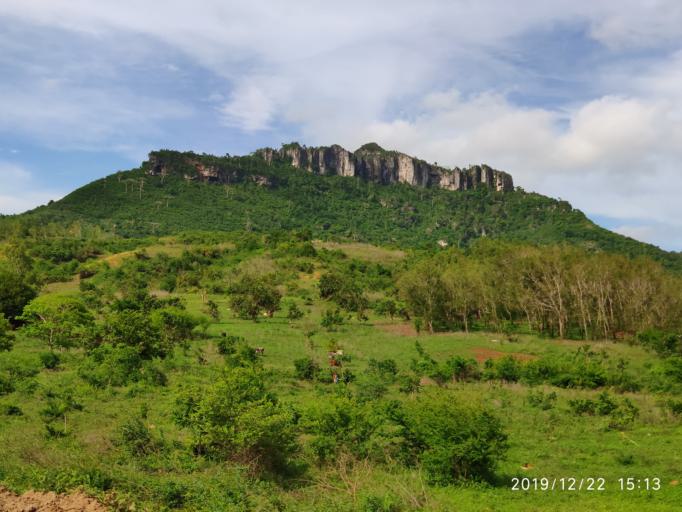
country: MG
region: Diana
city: Antsiranana
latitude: -12.4034
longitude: 49.3272
